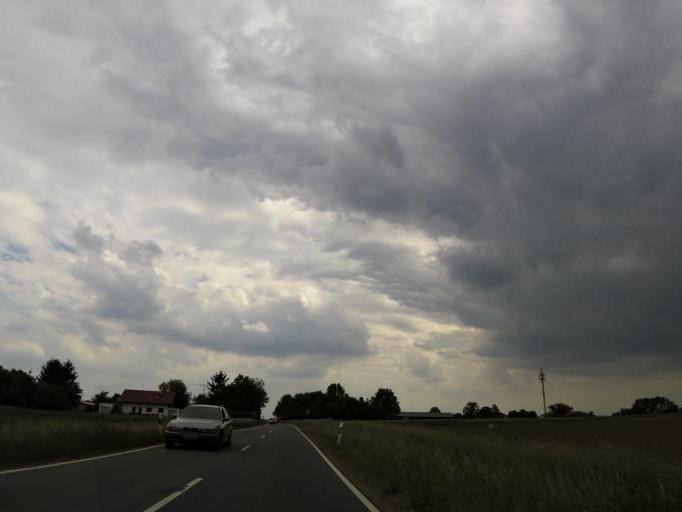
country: DE
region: Hesse
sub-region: Regierungsbezirk Darmstadt
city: Messel
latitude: 49.9484
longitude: 8.7427
